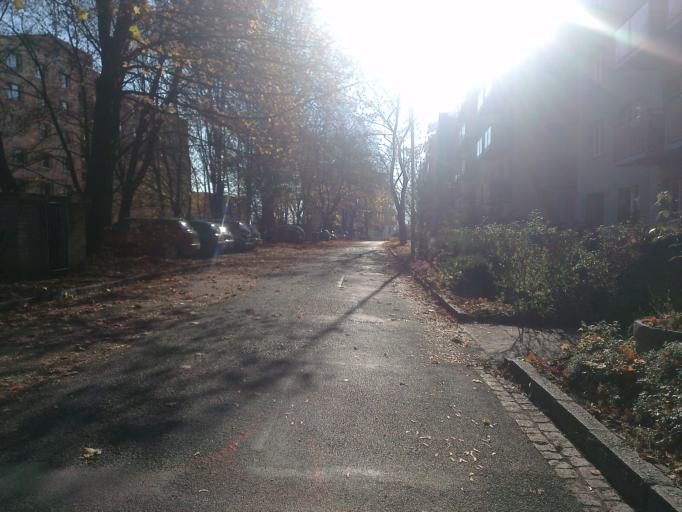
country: CZ
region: South Moravian
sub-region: Mesto Brno
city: Brno
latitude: 49.2166
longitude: 16.6293
